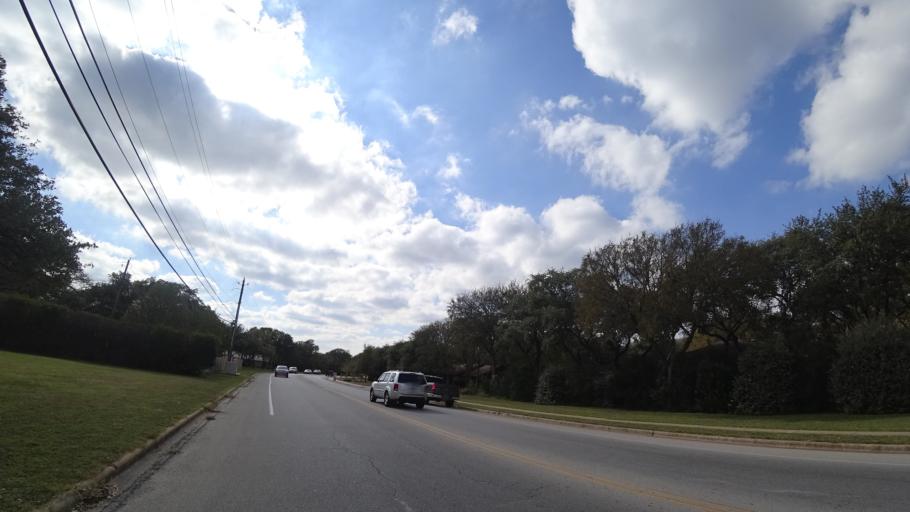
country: US
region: Texas
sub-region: Travis County
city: Shady Hollow
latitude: 30.1717
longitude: -97.8574
